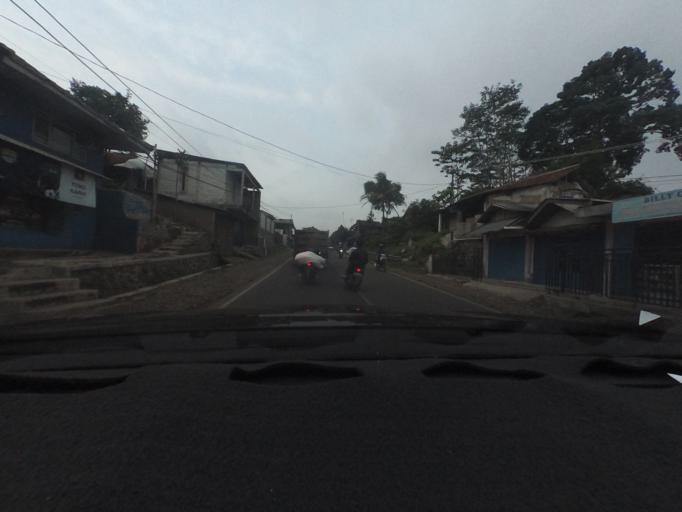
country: ID
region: West Java
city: Cicurug
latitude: -6.8113
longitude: 106.7694
